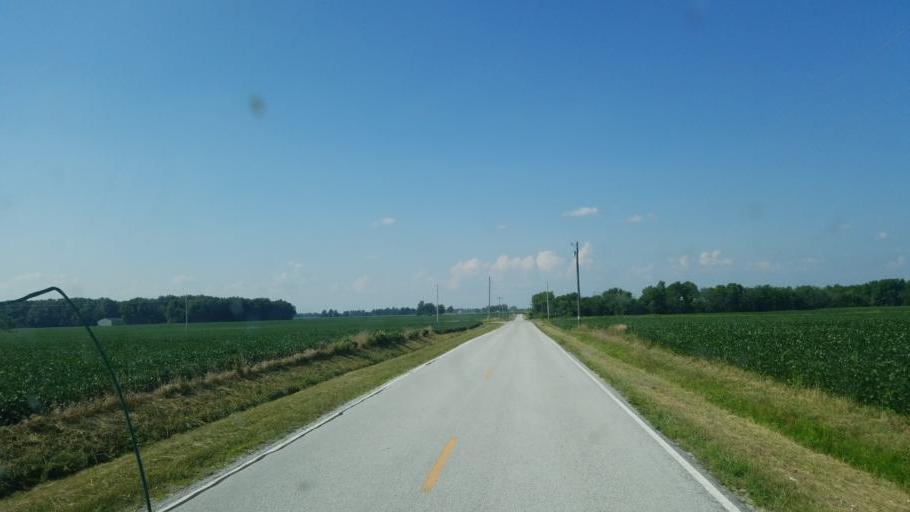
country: US
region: Ohio
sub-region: Hardin County
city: Forest
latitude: 40.7219
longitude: -83.4957
